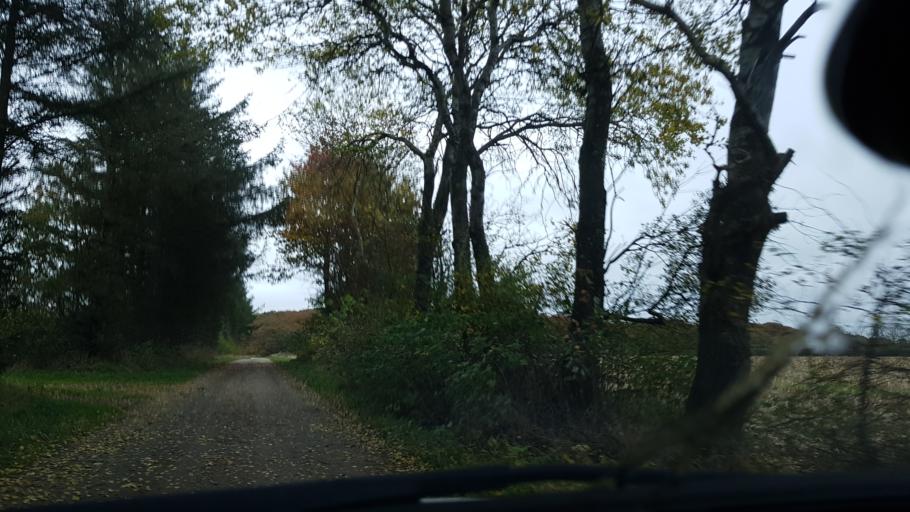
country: DK
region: South Denmark
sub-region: Esbjerg Kommune
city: Ribe
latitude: 55.3010
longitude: 8.8150
